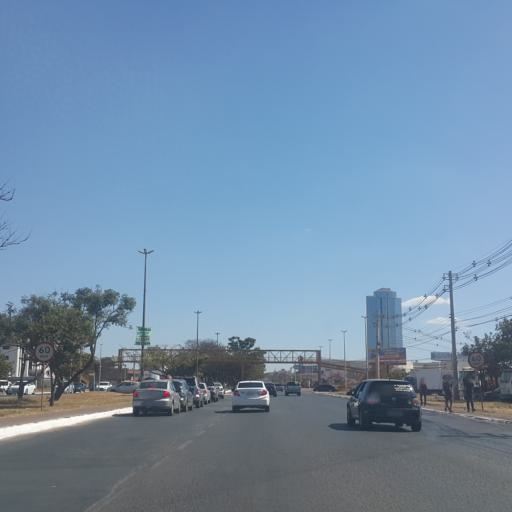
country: BR
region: Federal District
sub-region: Brasilia
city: Brasilia
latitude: -15.8084
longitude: -48.0847
